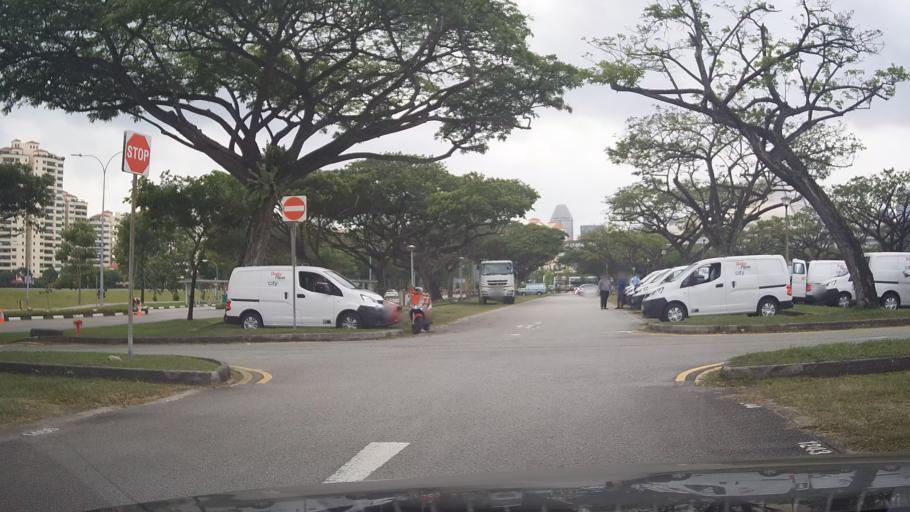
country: SG
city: Singapore
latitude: 1.3012
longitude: 103.8776
